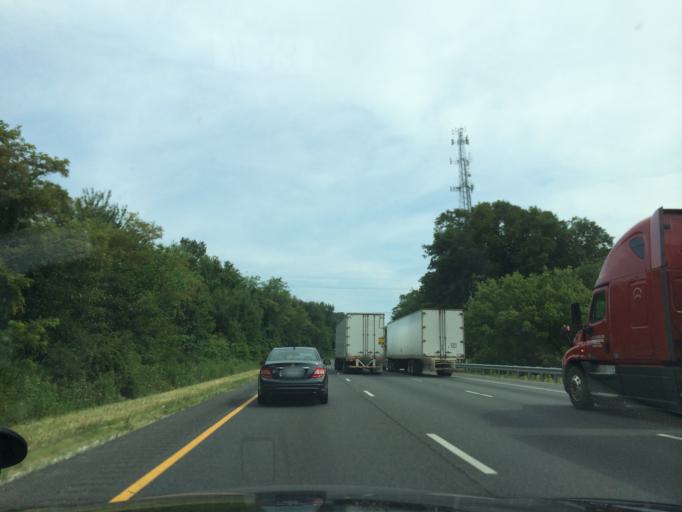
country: US
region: Maryland
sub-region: Frederick County
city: Myersville
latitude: 39.5426
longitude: -77.6071
